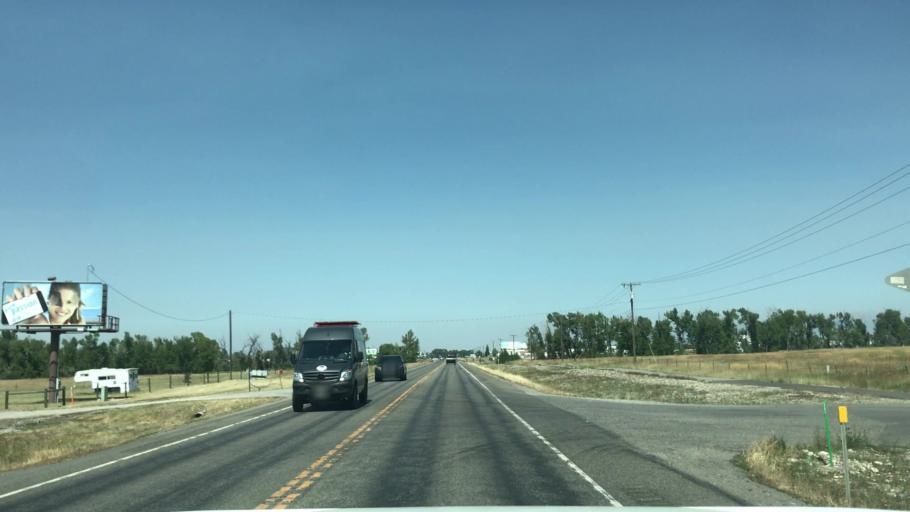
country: US
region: Montana
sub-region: Gallatin County
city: Four Corners
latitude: 45.5947
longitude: -111.1968
